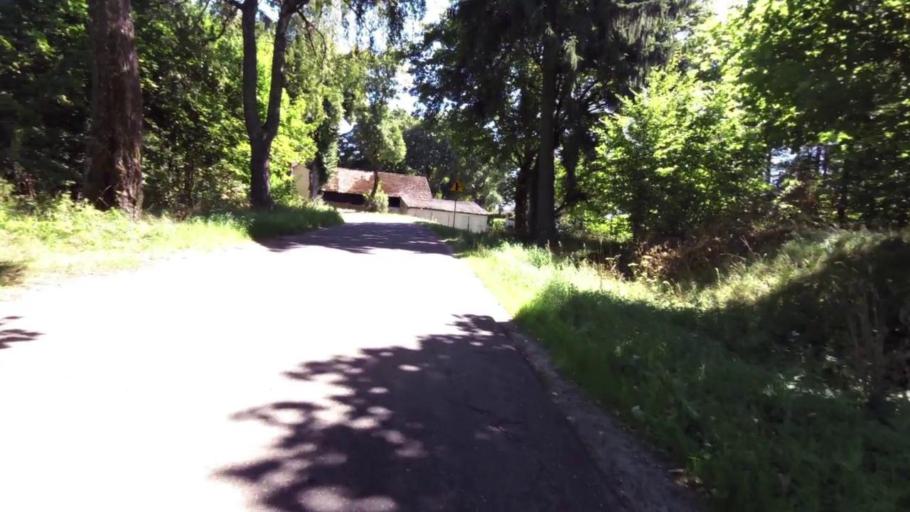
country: PL
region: West Pomeranian Voivodeship
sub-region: Powiat szczecinecki
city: Bialy Bor
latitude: 53.9562
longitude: 16.8434
